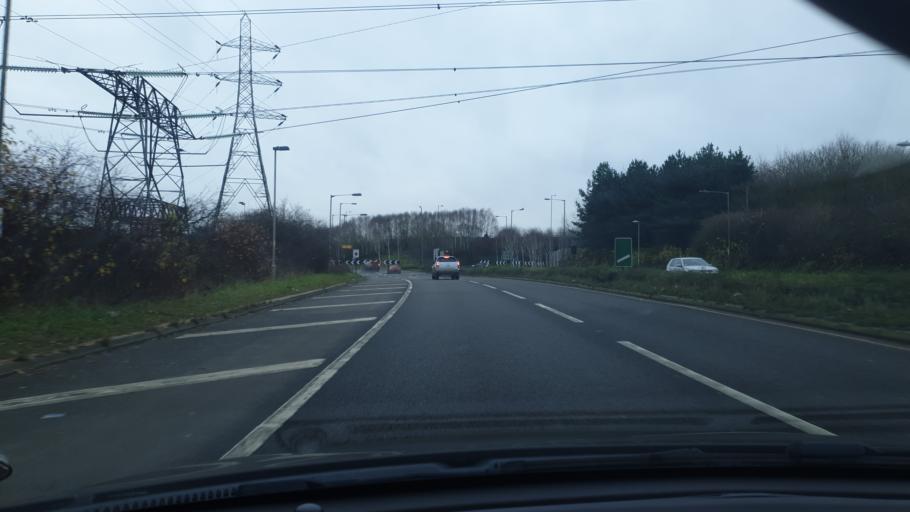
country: GB
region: England
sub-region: Walsall
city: Willenhall
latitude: 52.5757
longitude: -2.0495
